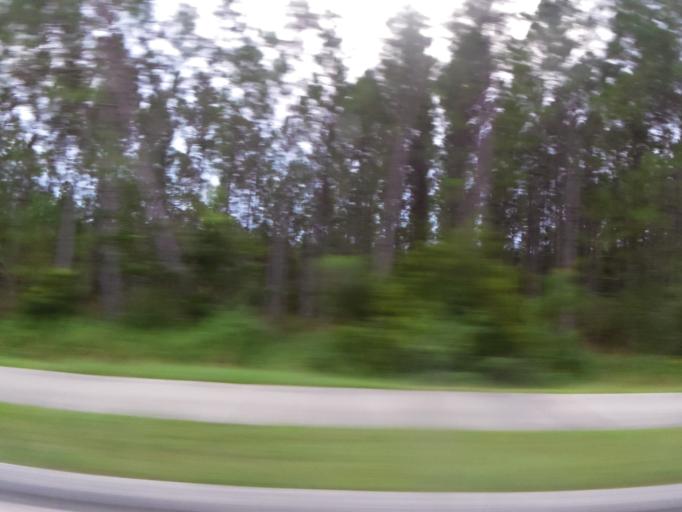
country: US
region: Florida
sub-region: Saint Johns County
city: Fruit Cove
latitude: 30.0840
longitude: -81.5671
